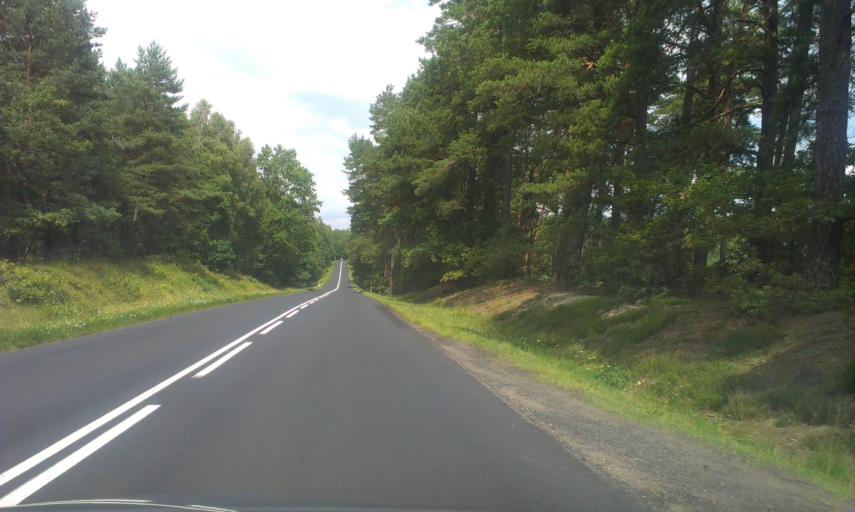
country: PL
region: West Pomeranian Voivodeship
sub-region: Powiat bialogardzki
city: Bialogard
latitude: 53.9405
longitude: 16.0603
